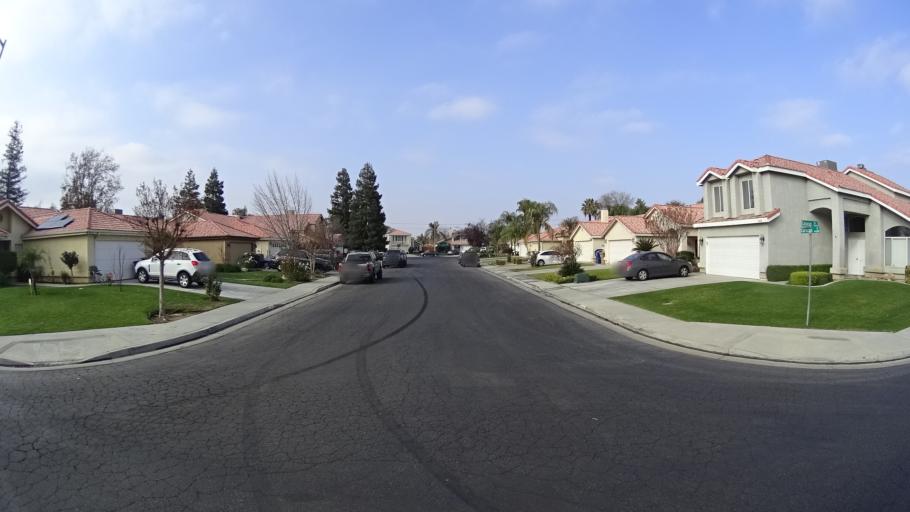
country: US
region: California
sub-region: Kern County
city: Greenfield
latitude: 35.3052
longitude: -119.0727
